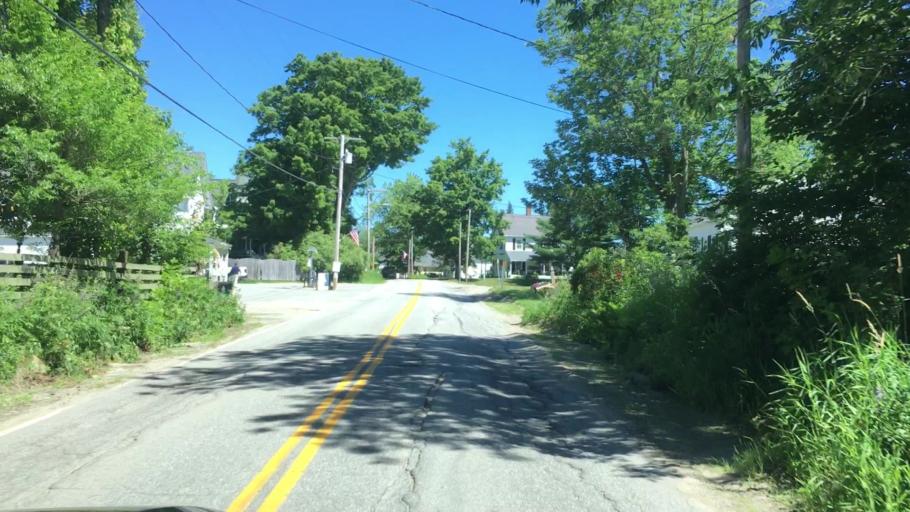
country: US
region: Maine
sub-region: Hancock County
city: Penobscot
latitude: 44.4539
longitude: -68.7025
